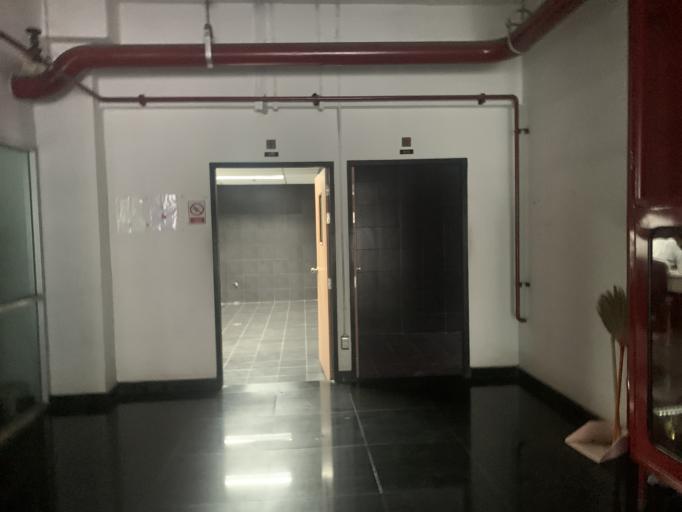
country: TH
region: Bangkok
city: Chatuchak
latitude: 13.8454
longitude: 100.5695
